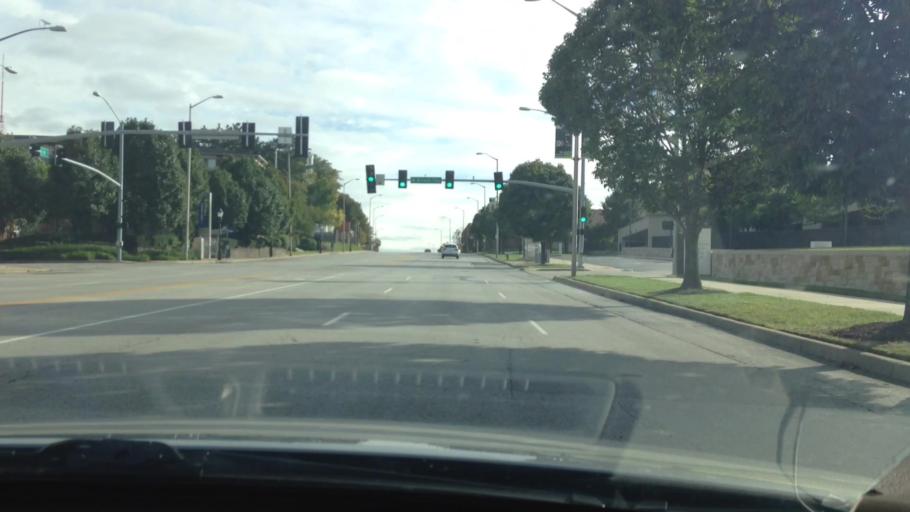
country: US
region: Missouri
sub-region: Jackson County
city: Kansas City
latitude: 39.0753
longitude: -94.5851
